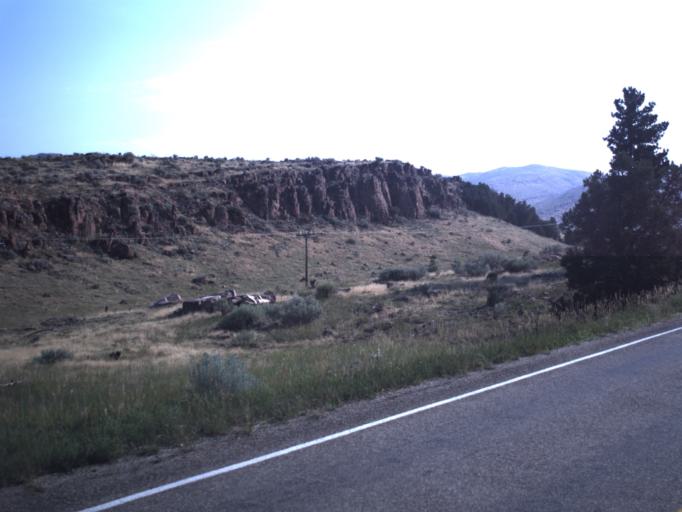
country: US
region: Utah
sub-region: Daggett County
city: Manila
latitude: 40.9315
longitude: -109.4078
